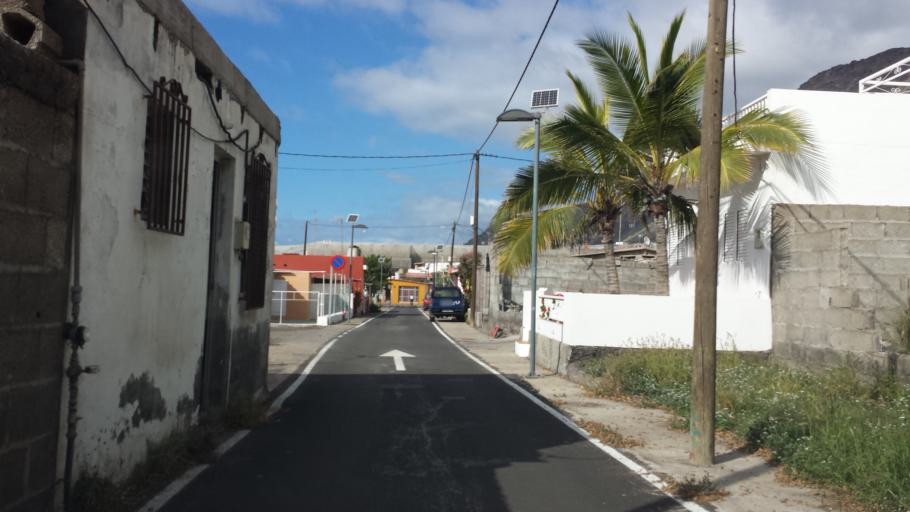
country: ES
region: Canary Islands
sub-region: Provincia de Santa Cruz de Tenerife
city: Fuencaliente de la Palma
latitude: 28.5527
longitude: -17.8884
